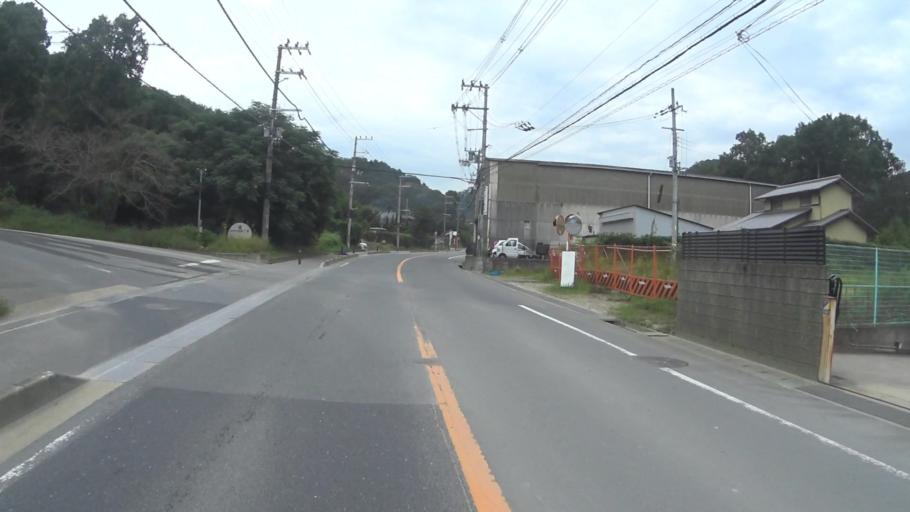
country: JP
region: Kyoto
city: Tanabe
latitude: 34.8327
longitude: 135.8211
